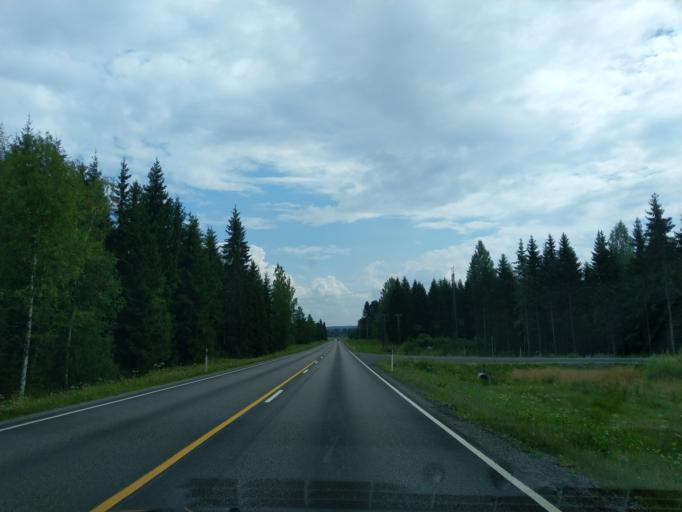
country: FI
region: South Karelia
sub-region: Imatra
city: Parikkala
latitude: 61.6119
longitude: 29.4535
